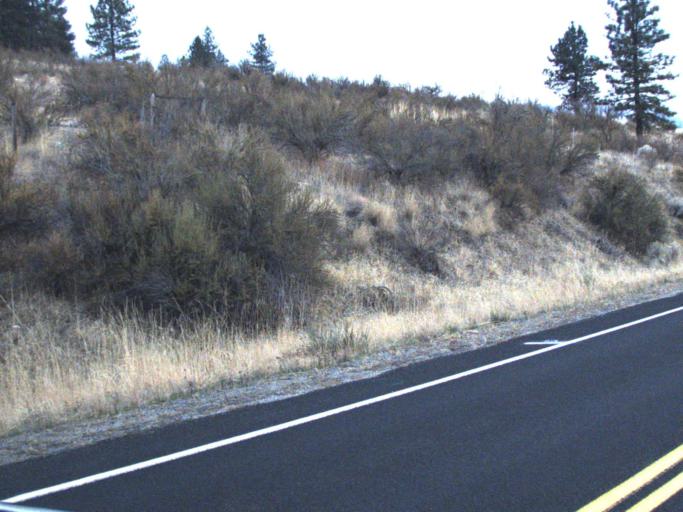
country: US
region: Washington
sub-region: Lincoln County
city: Davenport
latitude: 47.9213
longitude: -118.3303
